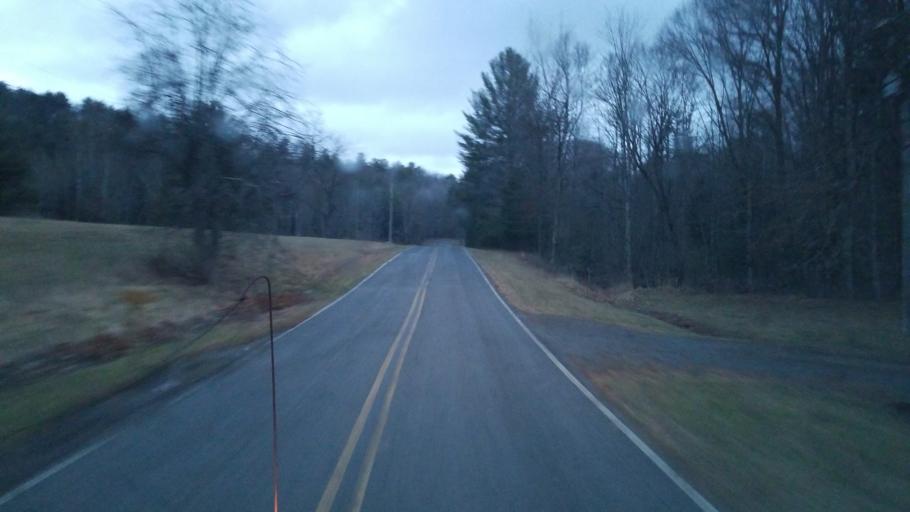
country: US
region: Virginia
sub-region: Pulaski County
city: Pulaski
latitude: 37.1164
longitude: -80.8779
